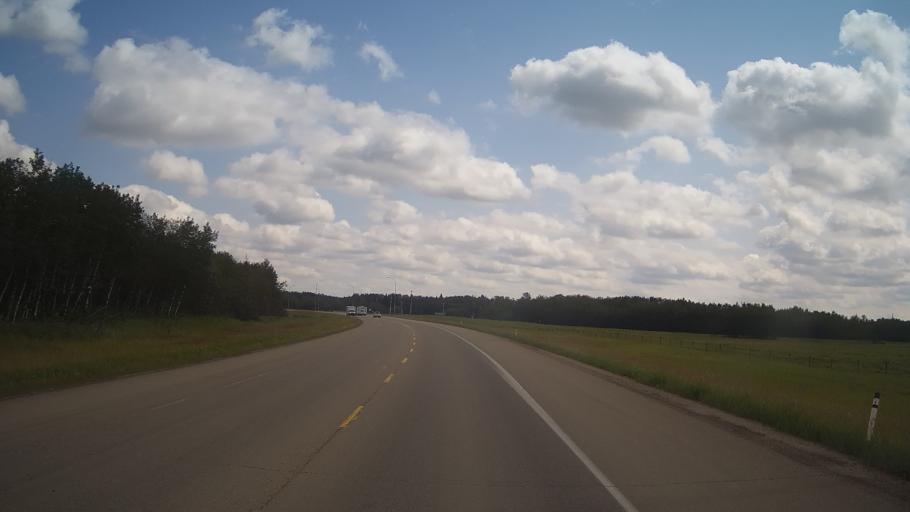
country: CA
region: Alberta
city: Sherwood Park
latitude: 53.3977
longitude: -113.1040
